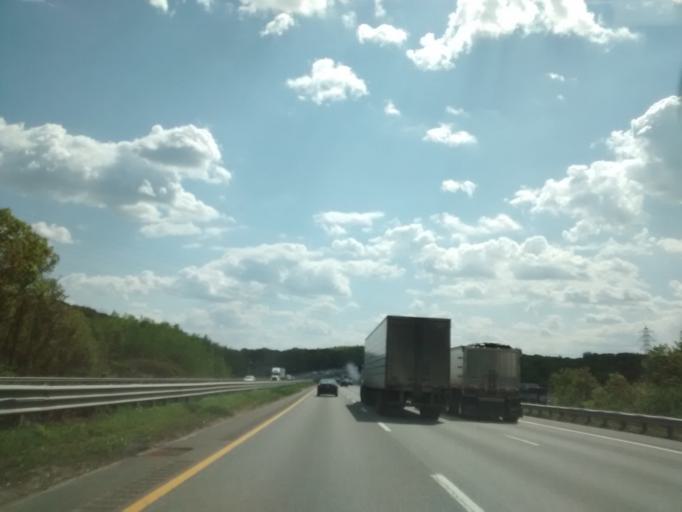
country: US
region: Massachusetts
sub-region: Worcester County
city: Auburn
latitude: 42.1991
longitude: -71.8395
